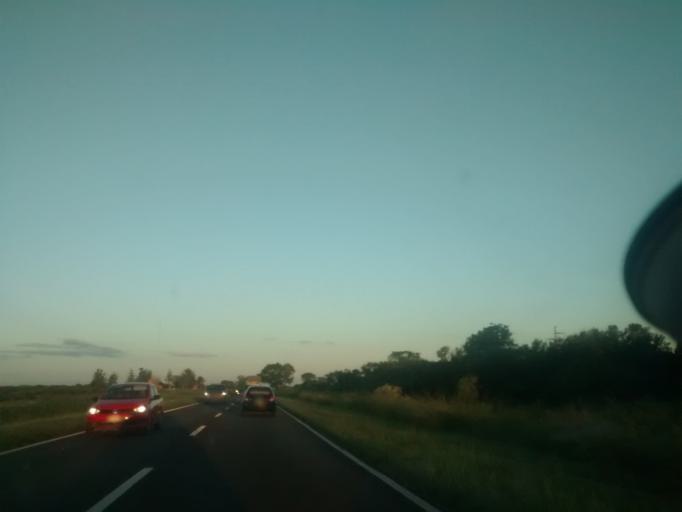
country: AR
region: Chaco
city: La Escondida
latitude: -27.1329
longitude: -59.4801
